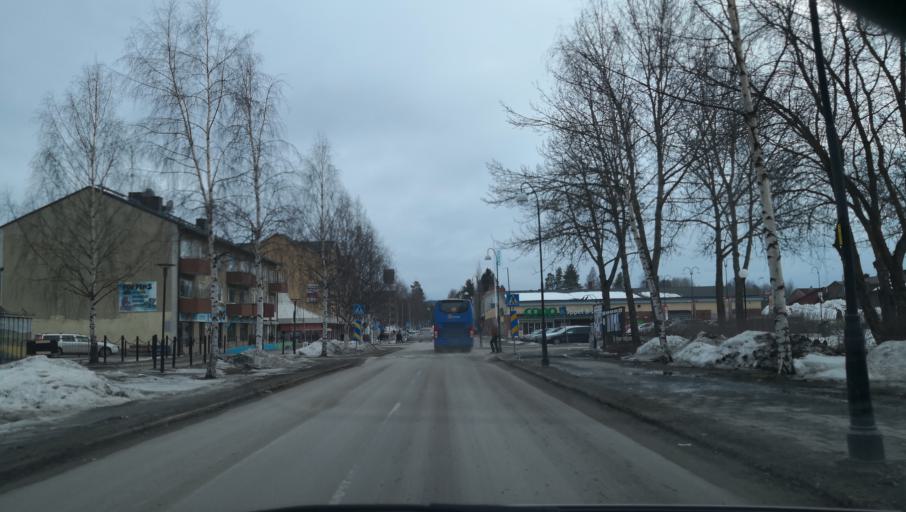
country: SE
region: Vaesterbotten
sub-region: Vannas Kommun
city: Vaennaes
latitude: 63.9082
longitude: 19.7516
